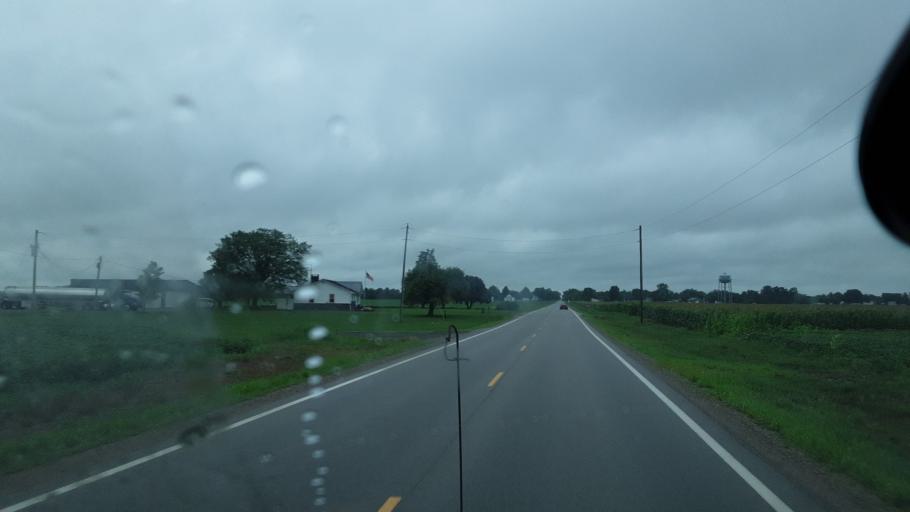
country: US
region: Ohio
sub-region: Mercer County
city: Rockford
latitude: 40.7588
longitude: -84.6257
